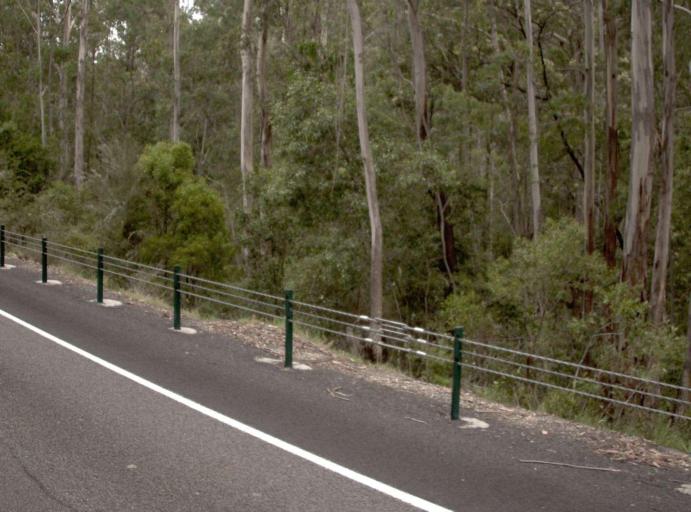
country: AU
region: New South Wales
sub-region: Bombala
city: Bombala
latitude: -37.2890
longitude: 149.2219
